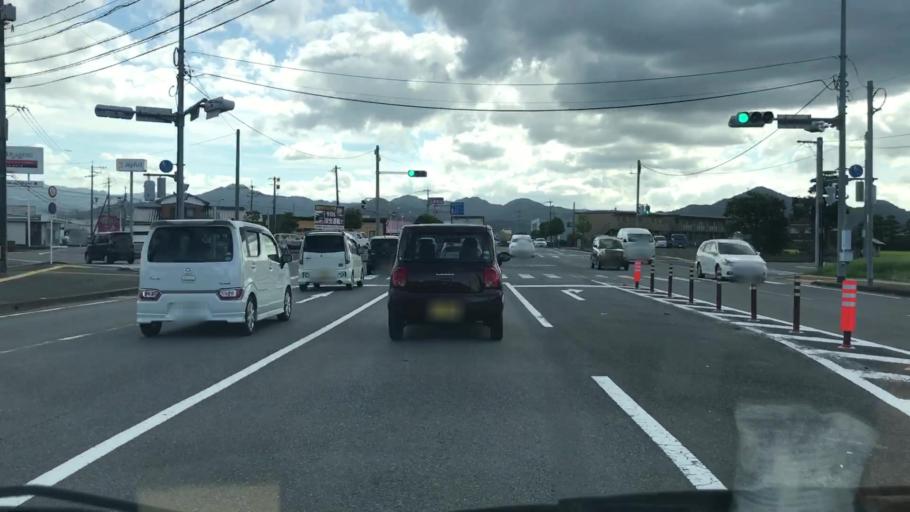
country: JP
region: Saga Prefecture
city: Kashima
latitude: 33.1275
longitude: 130.1036
